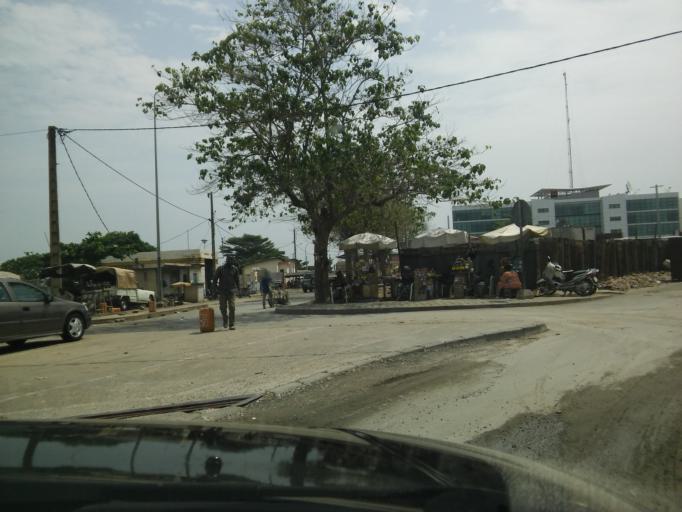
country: BJ
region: Littoral
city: Cotonou
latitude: 6.3587
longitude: 2.4395
